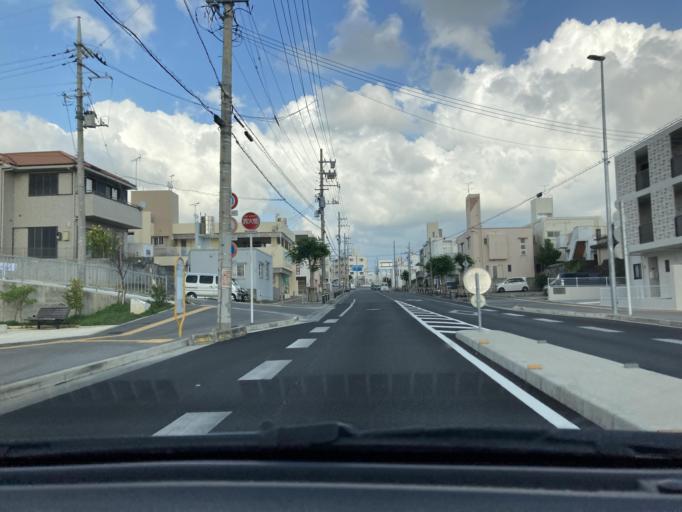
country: JP
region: Okinawa
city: Itoman
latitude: 26.1294
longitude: 127.6702
